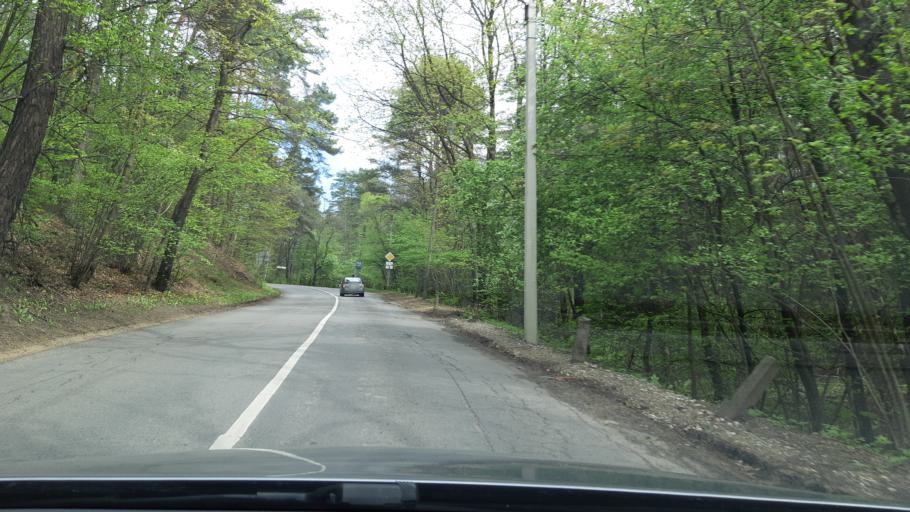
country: LT
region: Kauno apskritis
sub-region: Kauno rajonas
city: Akademija (Kaunas)
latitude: 54.9236
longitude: 23.8290
